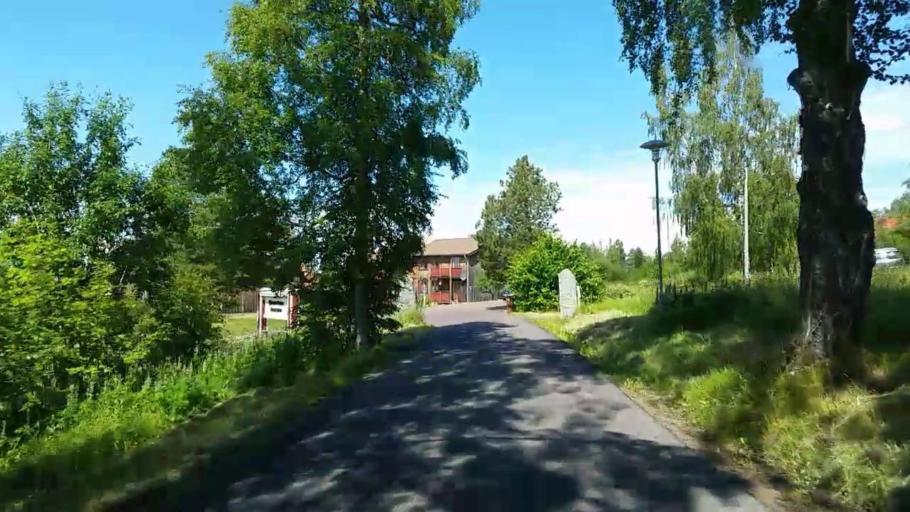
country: SE
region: Dalarna
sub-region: Leksand Municipality
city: Leksand
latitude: 60.8202
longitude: 14.9875
